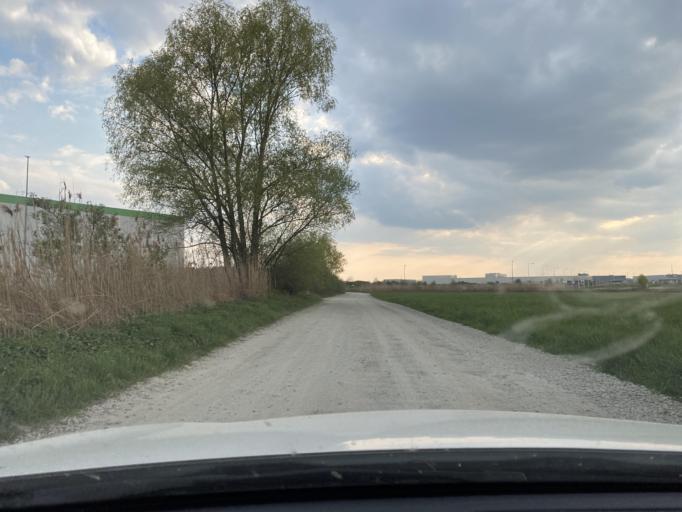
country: PL
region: Lower Silesian Voivodeship
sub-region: Powiat wroclawski
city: Mirkow
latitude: 51.1569
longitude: 17.1596
